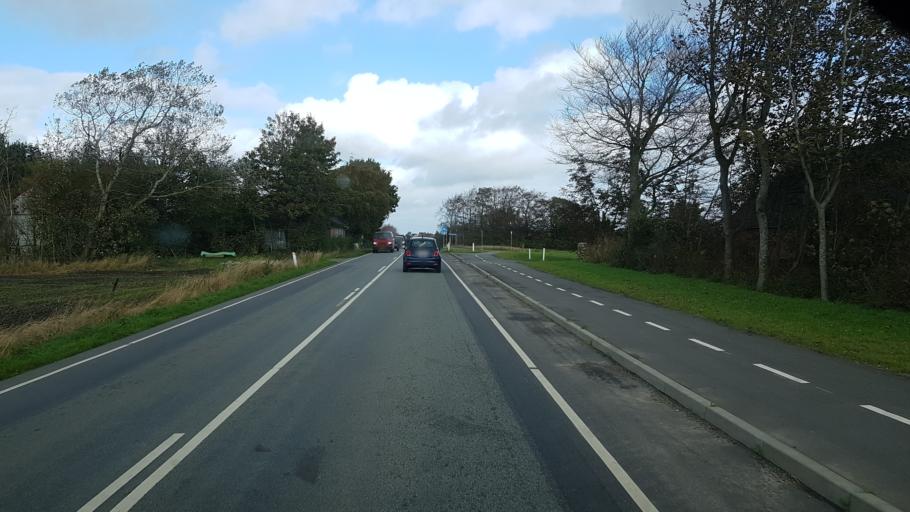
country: DK
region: South Denmark
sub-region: Vejen Kommune
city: Holsted
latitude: 55.4748
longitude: 8.9065
